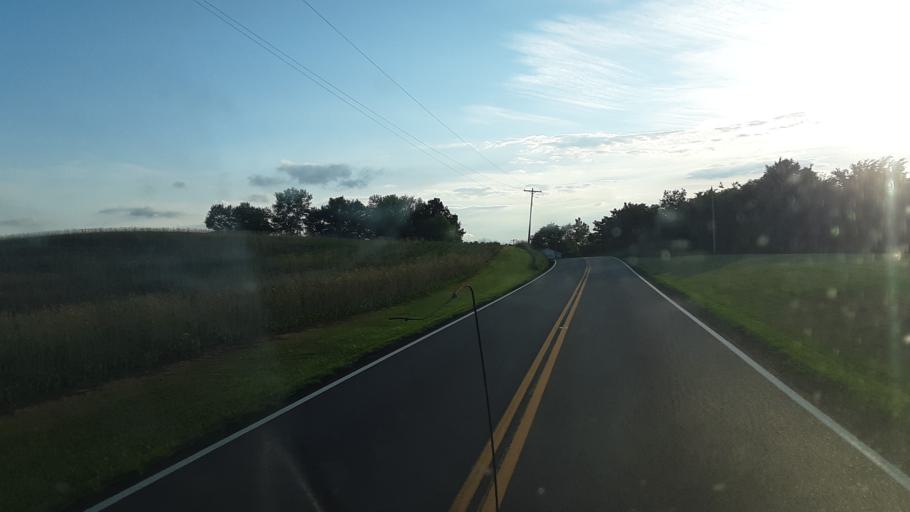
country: US
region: Ohio
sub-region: Harrison County
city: Cadiz
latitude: 40.3998
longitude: -80.9933
